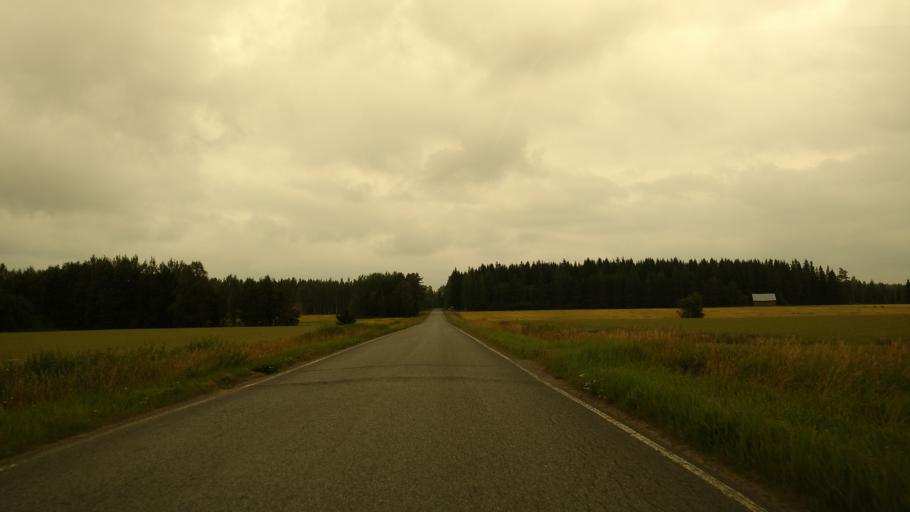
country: FI
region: Haeme
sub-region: Forssa
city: Ypaejae
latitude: 60.7549
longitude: 23.2080
